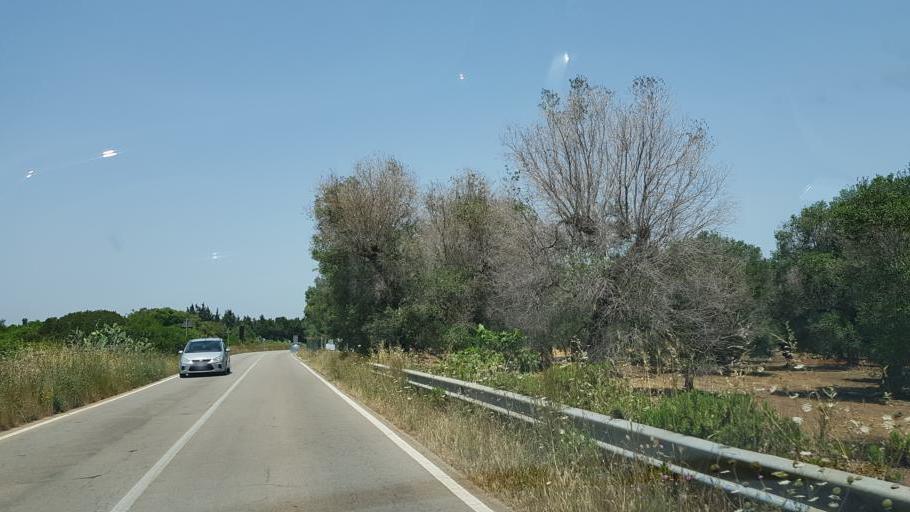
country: IT
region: Apulia
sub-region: Provincia di Lecce
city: Porto Cesareo
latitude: 40.3005
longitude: 17.9183
